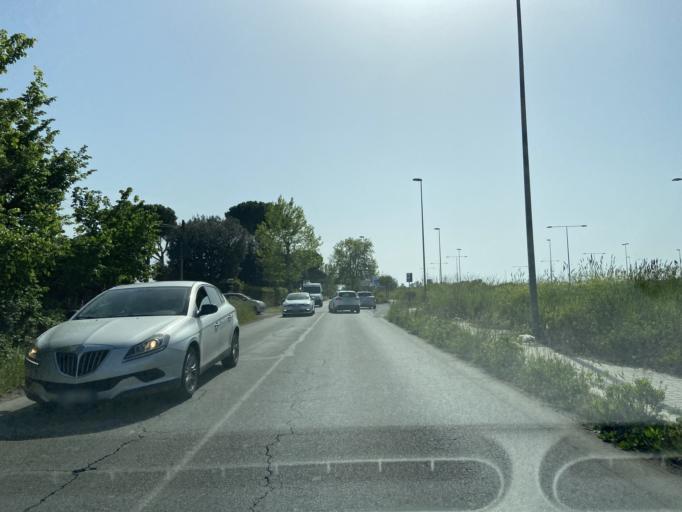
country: IT
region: Latium
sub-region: Citta metropolitana di Roma Capitale
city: Npp 23 (Parco Leonardo)
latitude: 41.7923
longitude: 12.2906
